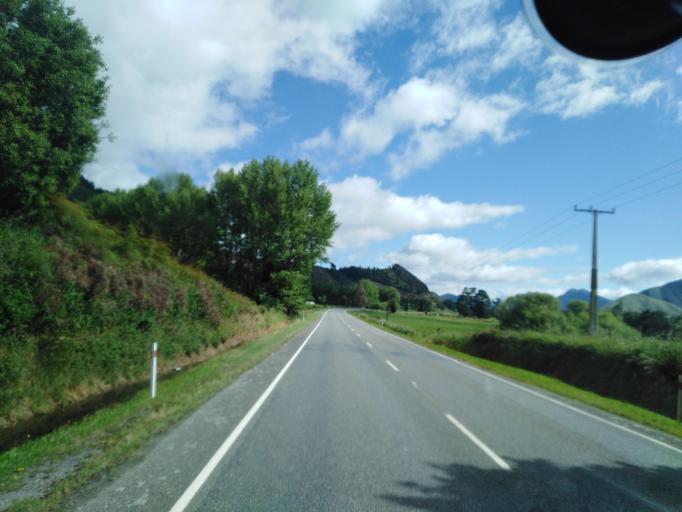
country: NZ
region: Nelson
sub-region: Nelson City
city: Nelson
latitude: -41.2703
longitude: 173.5726
